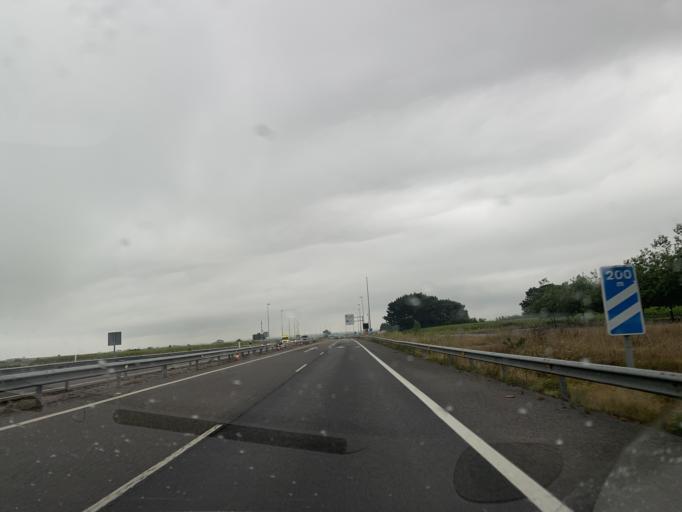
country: ES
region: Asturias
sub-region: Province of Asturias
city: Figueras
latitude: 43.5428
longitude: -7.0291
